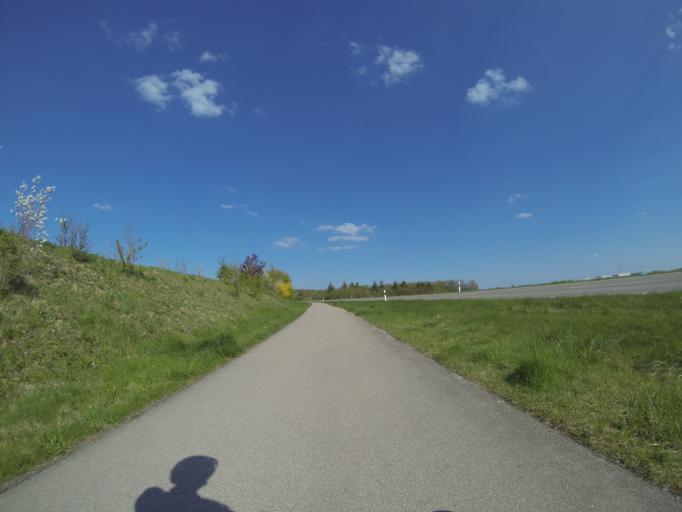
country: DE
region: Baden-Wuerttemberg
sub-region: Tuebingen Region
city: Laupheim
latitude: 48.2226
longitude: 9.8971
